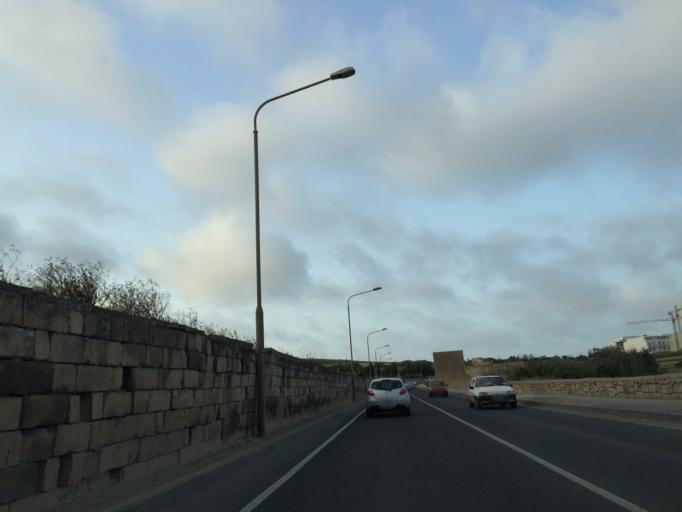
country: MT
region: Il-Mosta
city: Mosta
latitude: 35.9079
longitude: 14.4100
